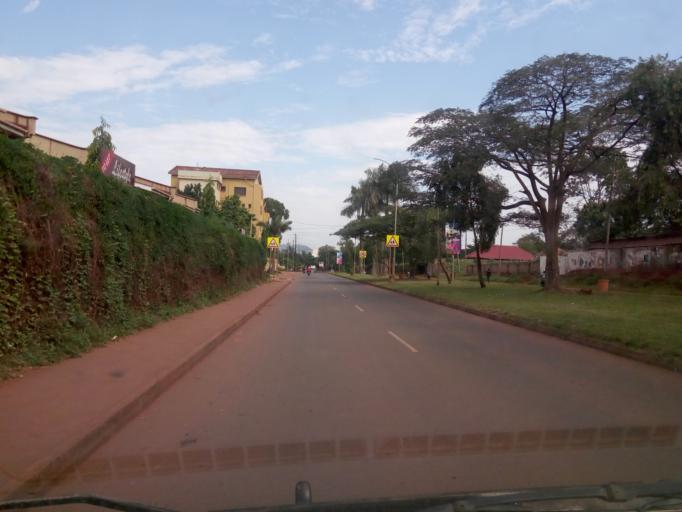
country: UG
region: Central Region
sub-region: Kampala District
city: Kampala
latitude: 0.3323
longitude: 32.6023
